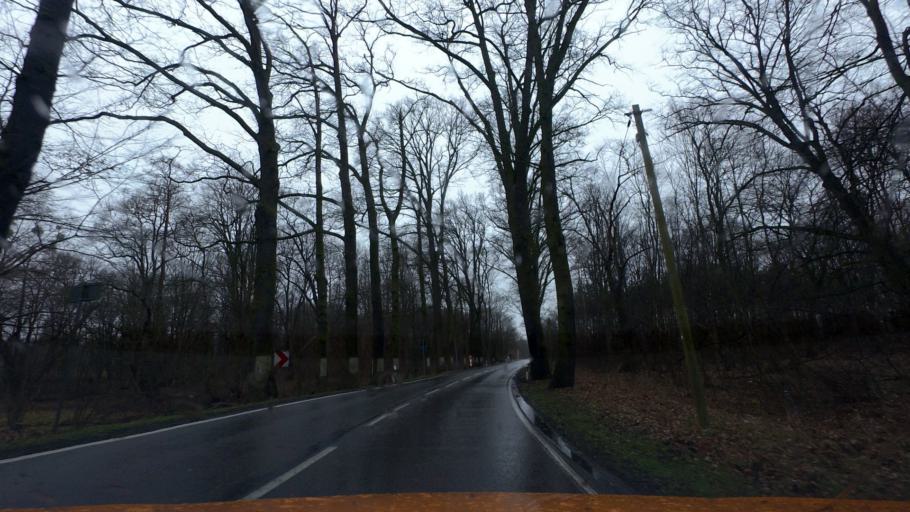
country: DE
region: Brandenburg
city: Dallgow-Doeberitz
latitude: 52.5923
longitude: 13.0505
